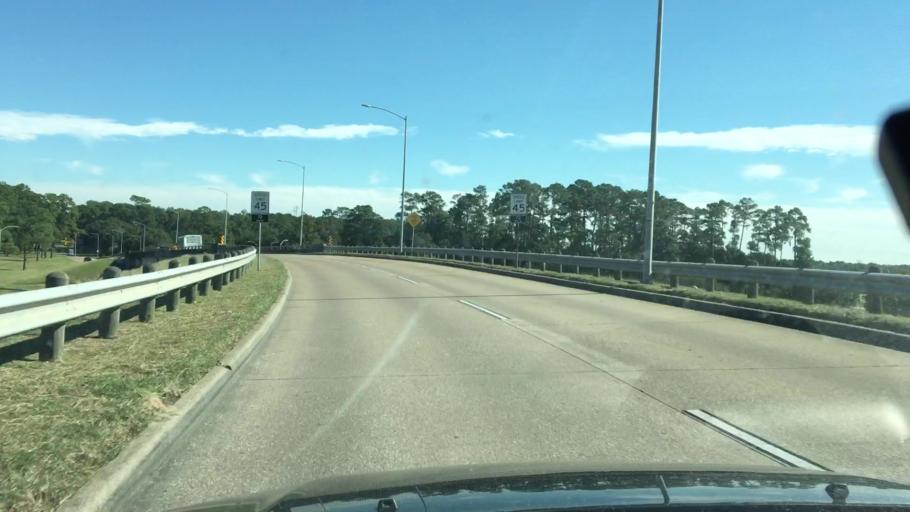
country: US
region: Texas
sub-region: Harris County
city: Humble
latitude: 29.9849
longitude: -95.3264
